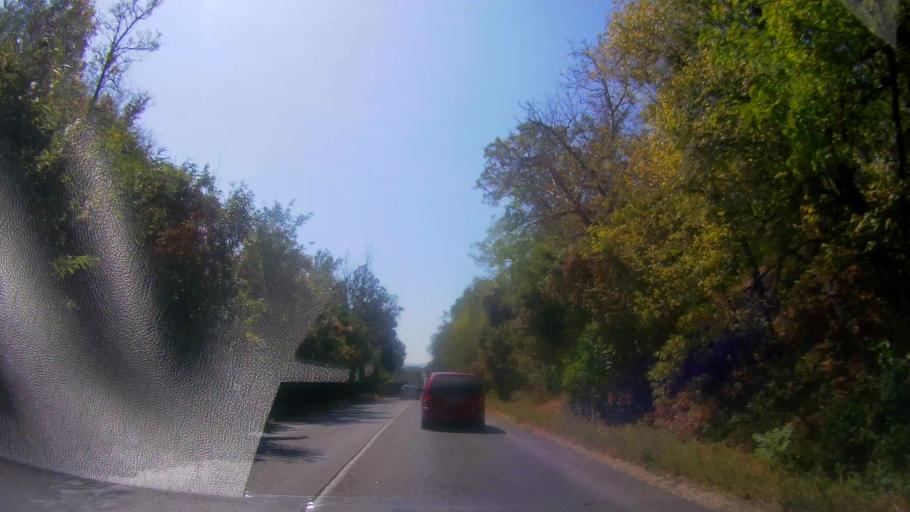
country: BG
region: Veliko Turnovo
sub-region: Obshtina Gorna Oryakhovitsa
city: Purvomaytsi
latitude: 43.2451
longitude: 25.6439
